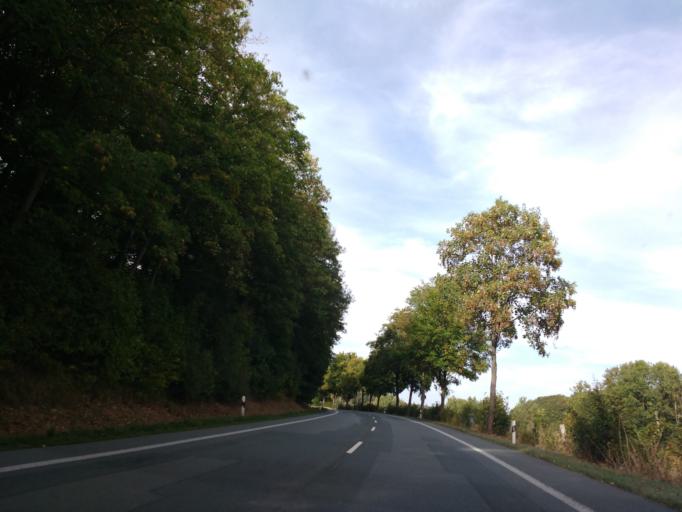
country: DE
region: North Rhine-Westphalia
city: Brakel
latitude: 51.6423
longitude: 9.1374
